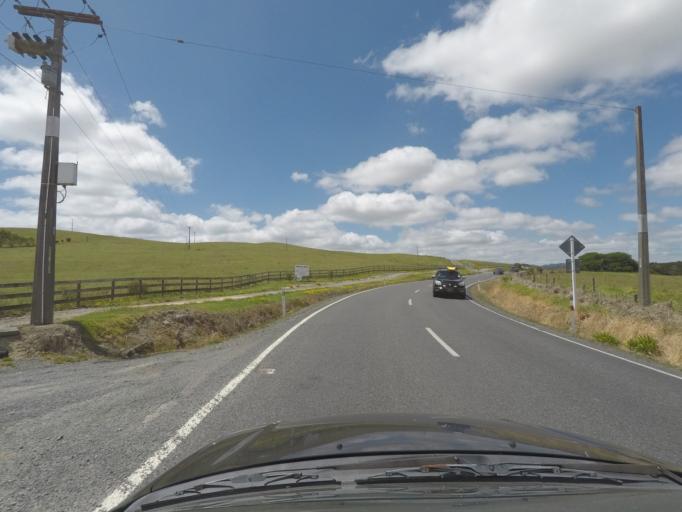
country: NZ
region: Northland
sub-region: Whangarei
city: Ruakaka
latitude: -35.9878
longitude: 174.4564
